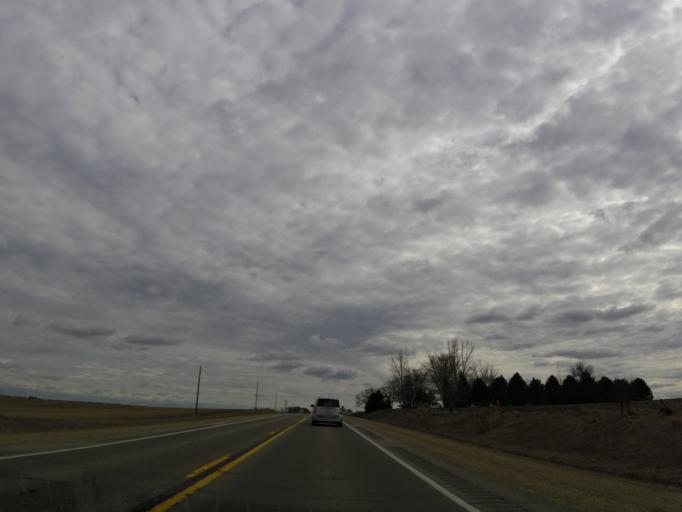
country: US
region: Iowa
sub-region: Chickasaw County
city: New Hampton
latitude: 43.1877
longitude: -92.2984
